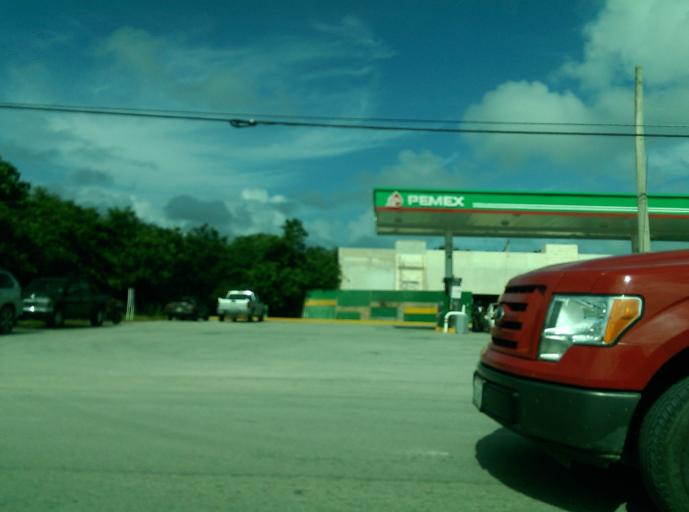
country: MX
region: Quintana Roo
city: Tulum
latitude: 20.2129
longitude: -87.4575
